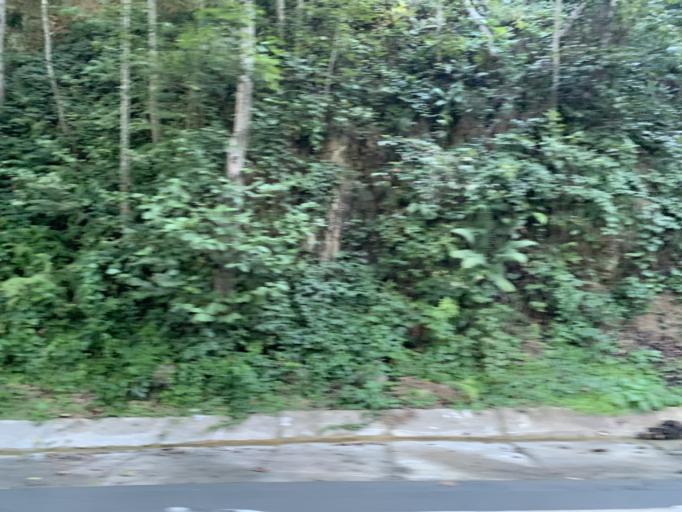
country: TR
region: Trabzon
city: Macka
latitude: 40.7062
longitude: 39.6501
